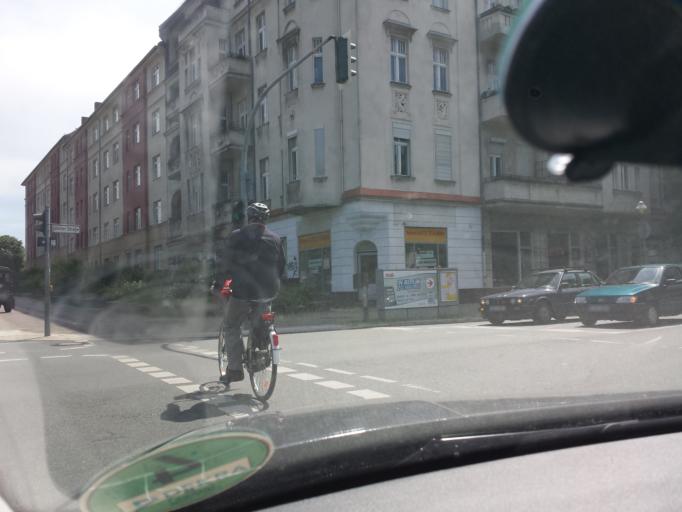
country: DE
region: Berlin
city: Gesundbrunnen
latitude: 52.5550
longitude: 13.3922
